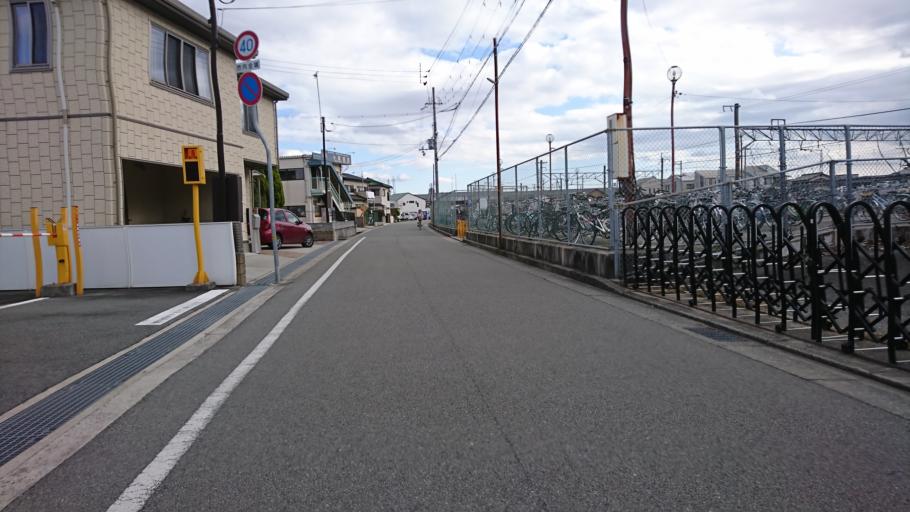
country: JP
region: Hyogo
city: Kakogawacho-honmachi
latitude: 34.7845
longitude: 134.8145
